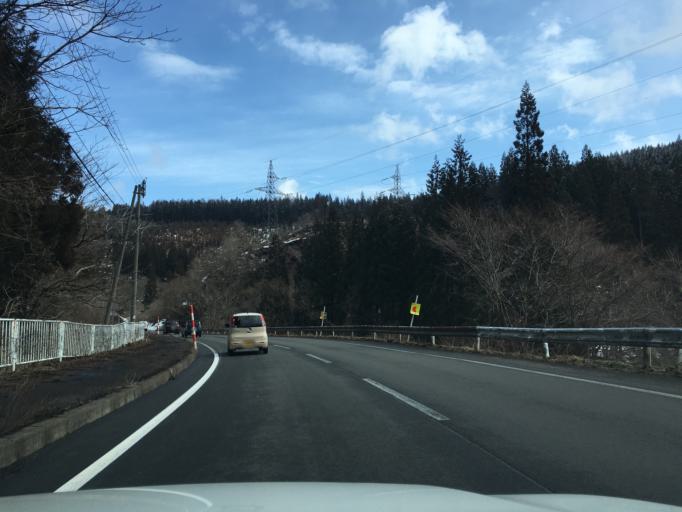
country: JP
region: Akita
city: Takanosu
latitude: 39.9990
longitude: 140.2715
